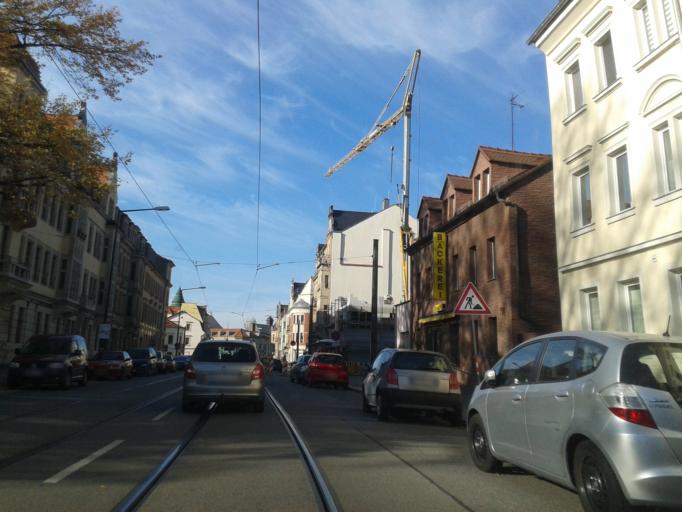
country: DE
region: Saxony
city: Dresden
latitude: 51.0831
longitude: 13.7115
